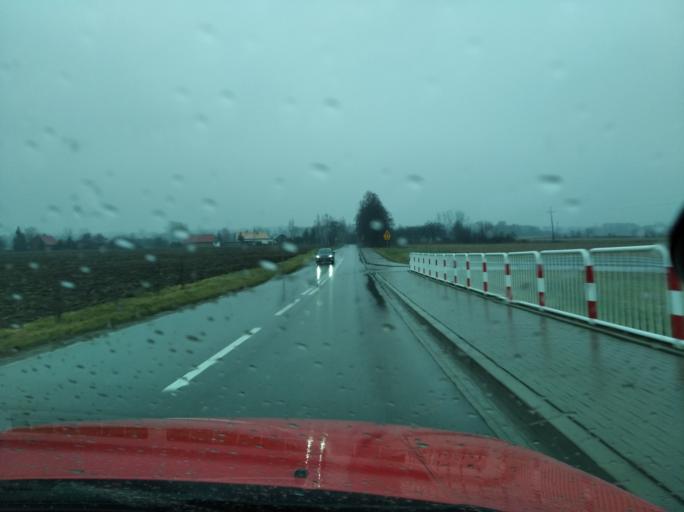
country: PL
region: Subcarpathian Voivodeship
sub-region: Powiat lancucki
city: Czarna
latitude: 50.0884
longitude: 22.1695
